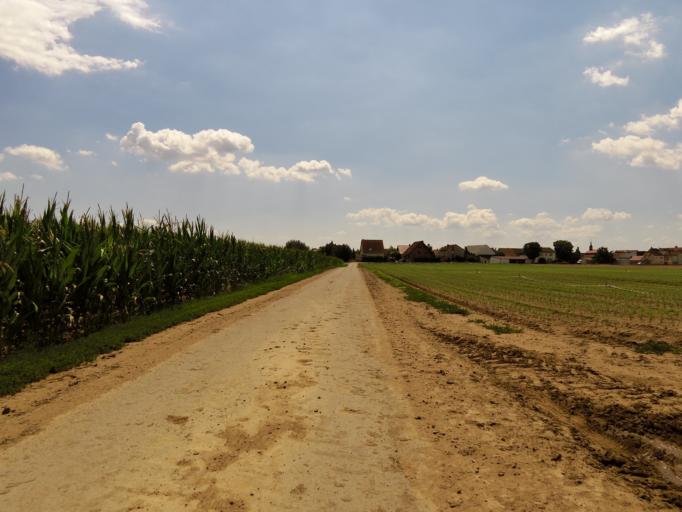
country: DE
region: Rheinland-Pfalz
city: Hochdorf-Assenheim
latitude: 49.4288
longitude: 8.2860
